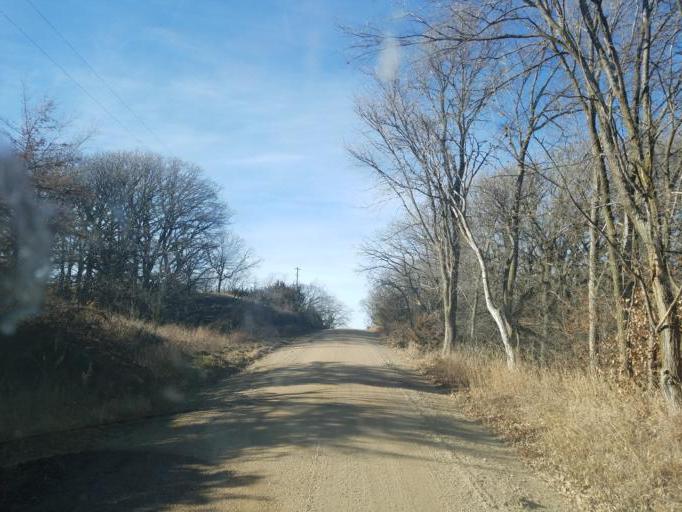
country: US
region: Nebraska
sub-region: Knox County
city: Center
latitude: 42.6554
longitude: -97.7977
